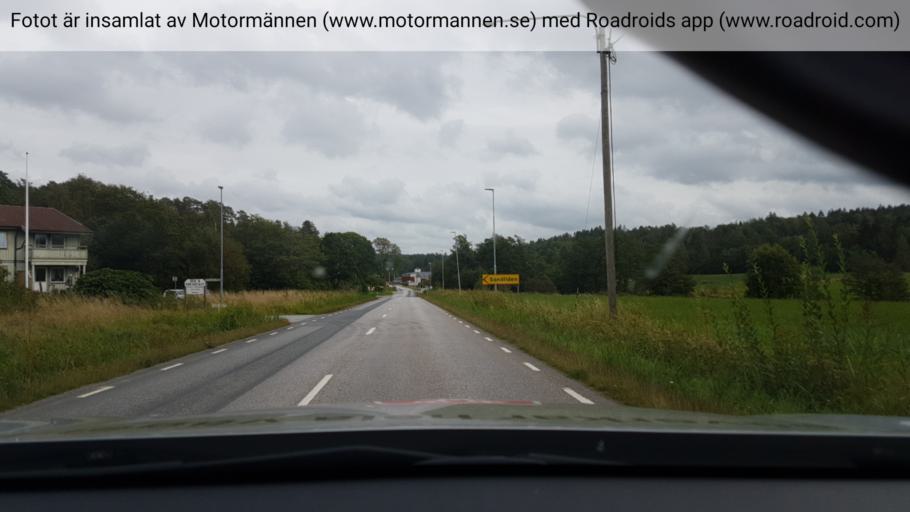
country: SE
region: Vaestra Goetaland
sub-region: Sotenas Kommun
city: Hunnebostrand
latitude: 58.5663
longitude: 11.3755
